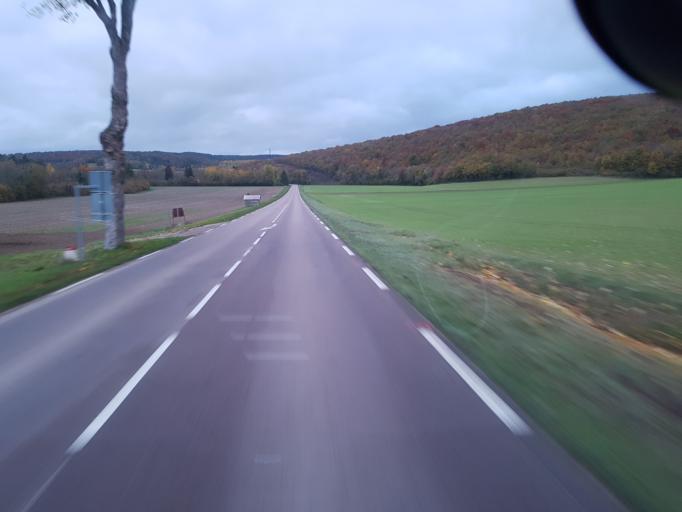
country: FR
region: Champagne-Ardenne
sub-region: Departement de l'Aube
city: Mussy-sur-Seine
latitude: 48.0041
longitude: 4.4743
